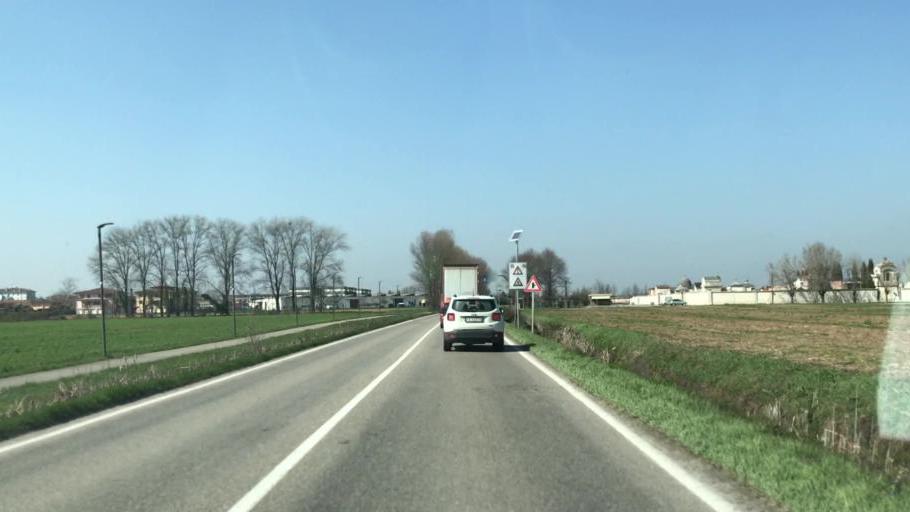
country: IT
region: Lombardy
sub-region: Provincia di Mantova
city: Cerese
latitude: 45.1163
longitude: 10.8069
